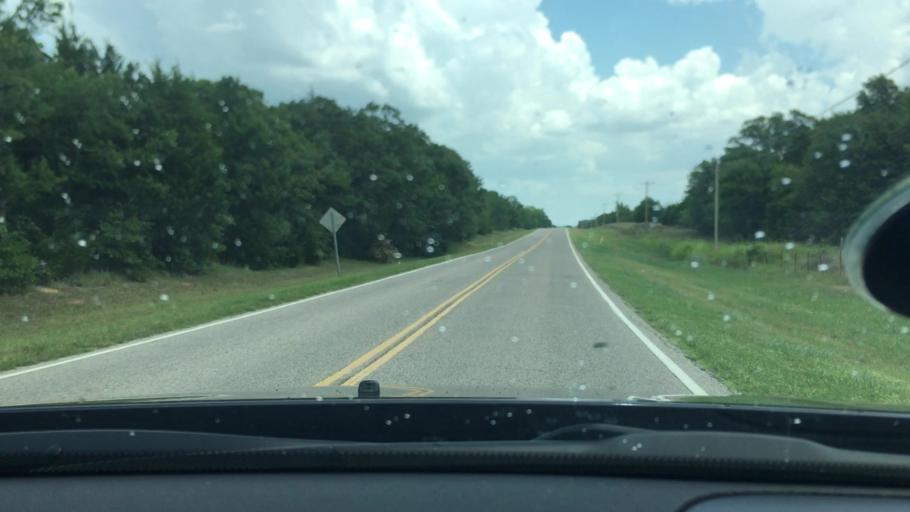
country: US
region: Oklahoma
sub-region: Love County
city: Marietta
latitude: 33.9694
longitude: -97.0191
